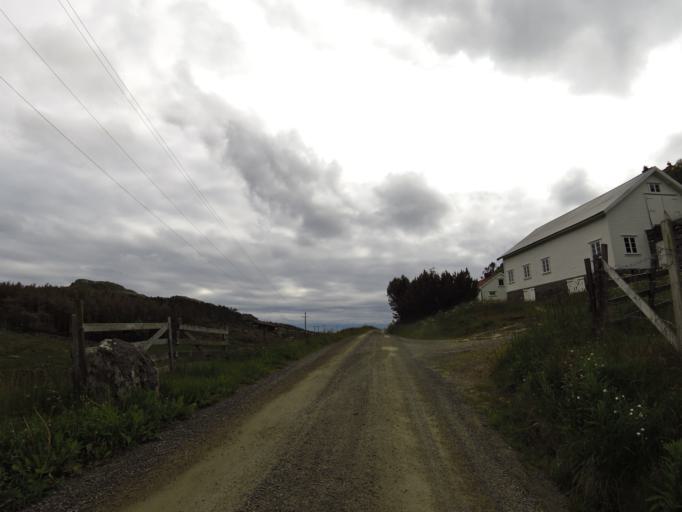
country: NO
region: Vest-Agder
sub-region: Farsund
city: Vestbygd
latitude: 58.1510
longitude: 6.6203
